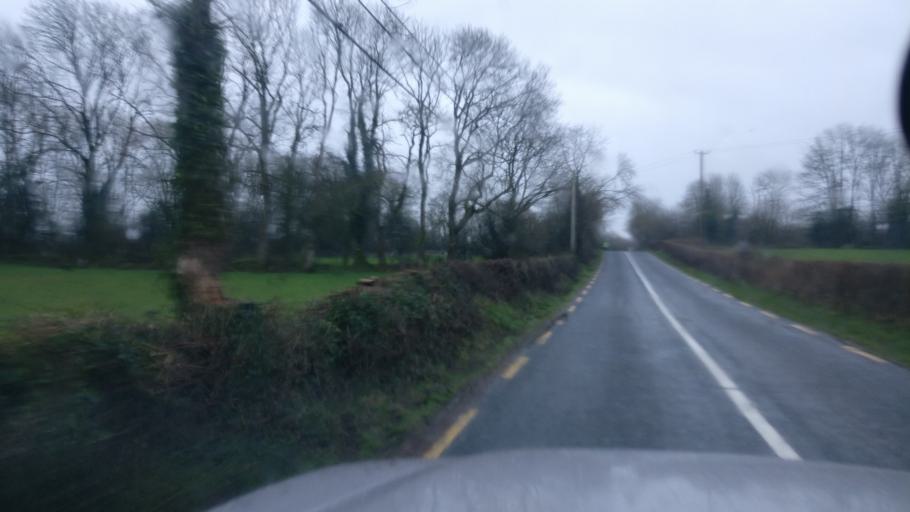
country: IE
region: Connaught
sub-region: County Galway
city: Ballinasloe
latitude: 53.2242
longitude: -8.1943
